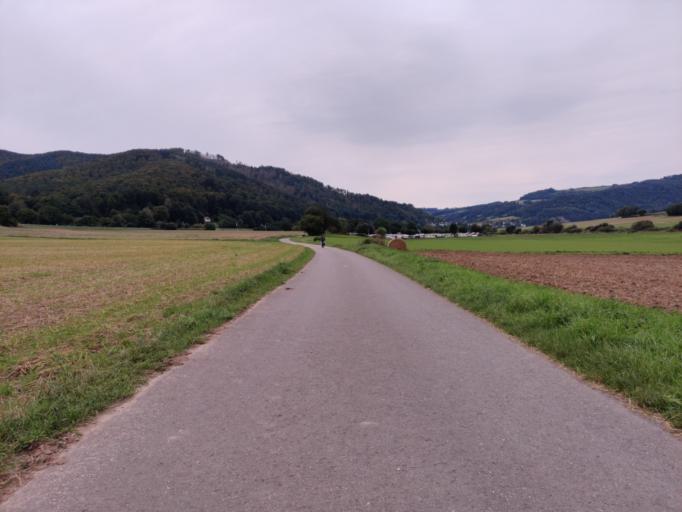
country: DE
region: Lower Saxony
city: Pegestorf
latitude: 51.9471
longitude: 9.5073
